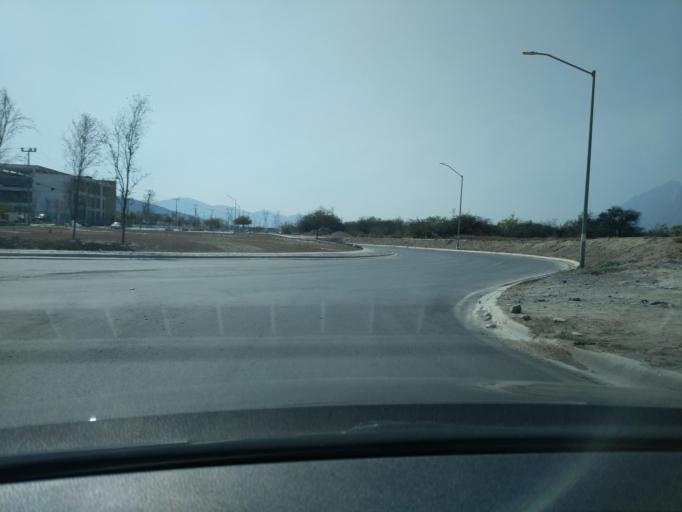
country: MX
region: Nuevo Leon
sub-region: Garcia
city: Los Parques
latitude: 25.7820
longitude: -100.4910
